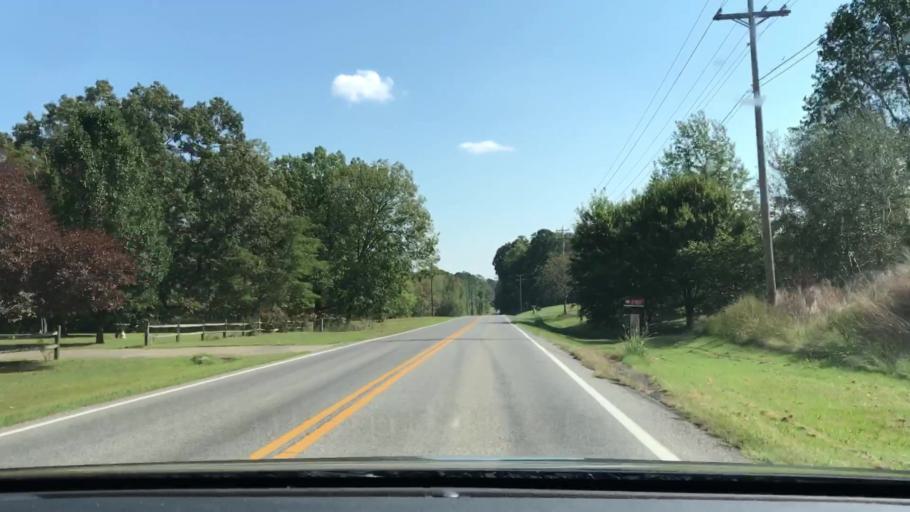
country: US
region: Kentucky
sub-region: Marshall County
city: Benton
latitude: 36.7644
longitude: -88.2535
